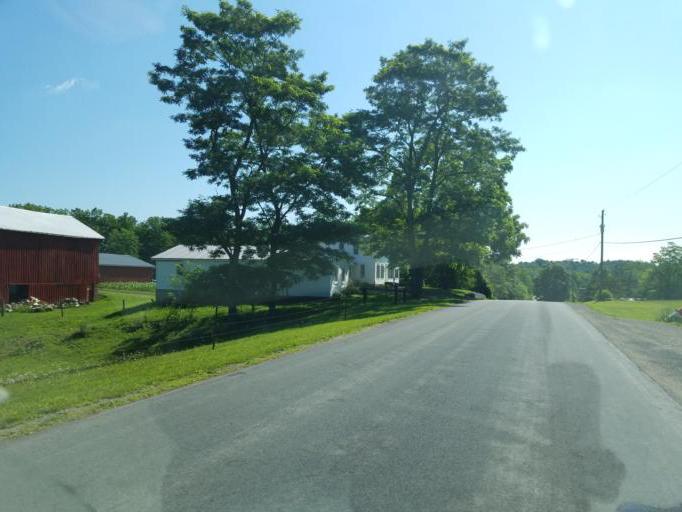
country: US
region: New York
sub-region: Wayne County
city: Clyde
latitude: 43.1135
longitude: -76.8471
